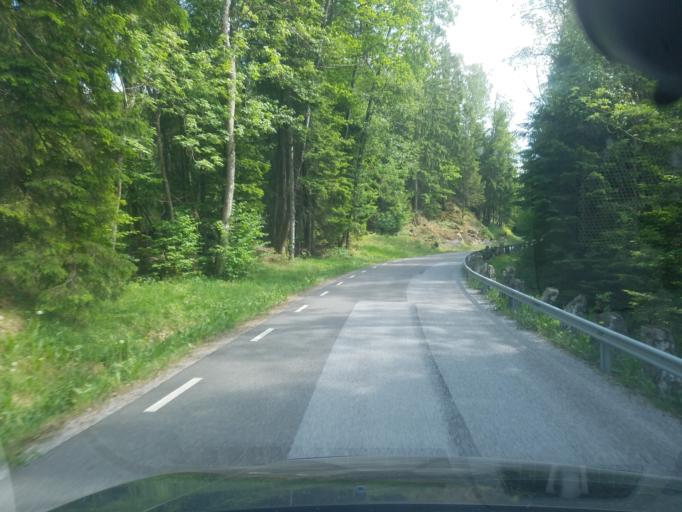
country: SE
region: Vaestra Goetaland
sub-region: Kungalvs Kommun
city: Diserod
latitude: 57.9680
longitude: 11.9911
